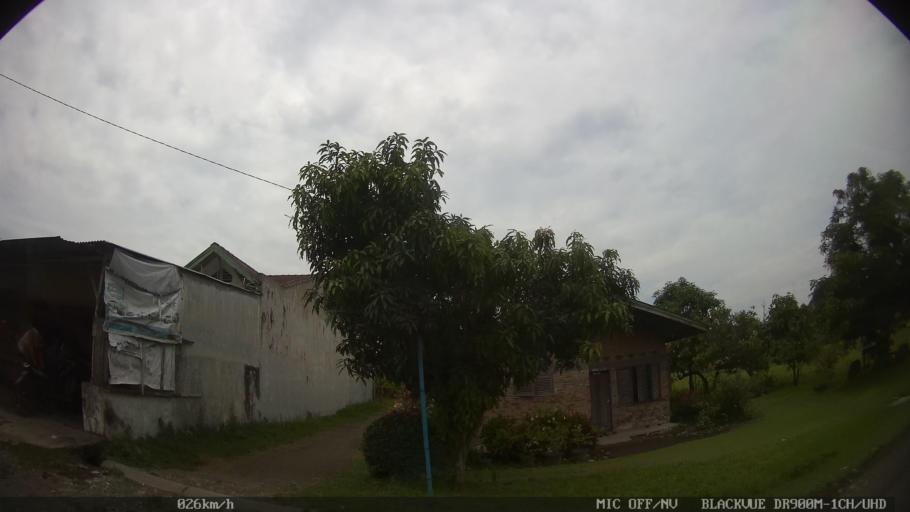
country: ID
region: North Sumatra
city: Sunggal
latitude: 3.6305
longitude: 98.5610
